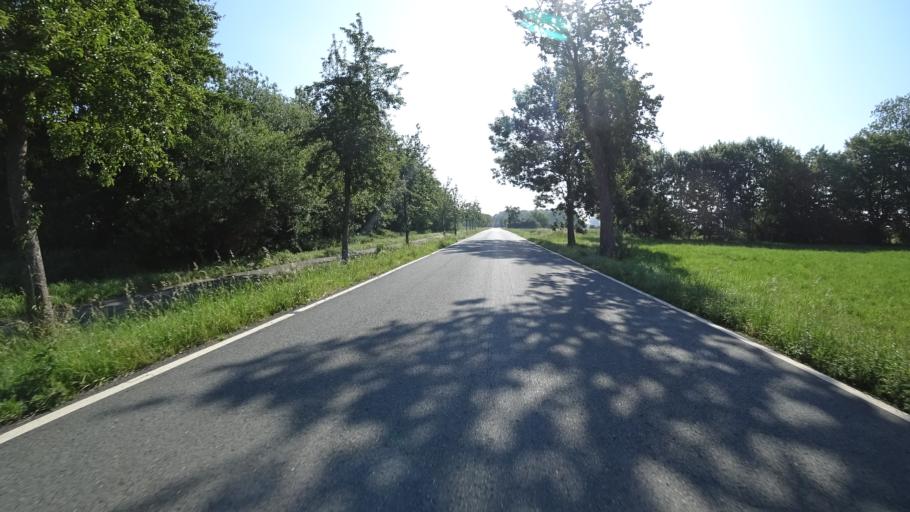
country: DE
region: North Rhine-Westphalia
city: Erwitte
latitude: 51.6322
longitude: 8.3773
